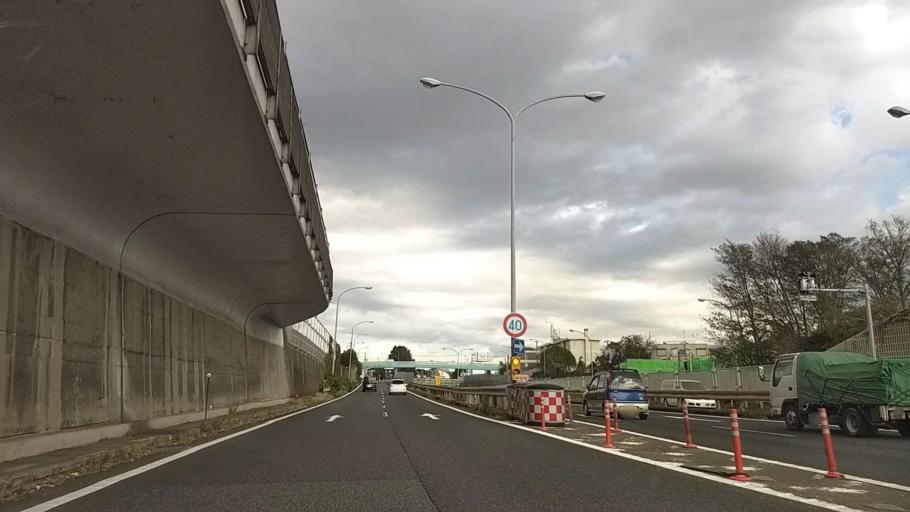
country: JP
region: Tokyo
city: Tokyo
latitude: 35.6057
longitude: 139.6387
